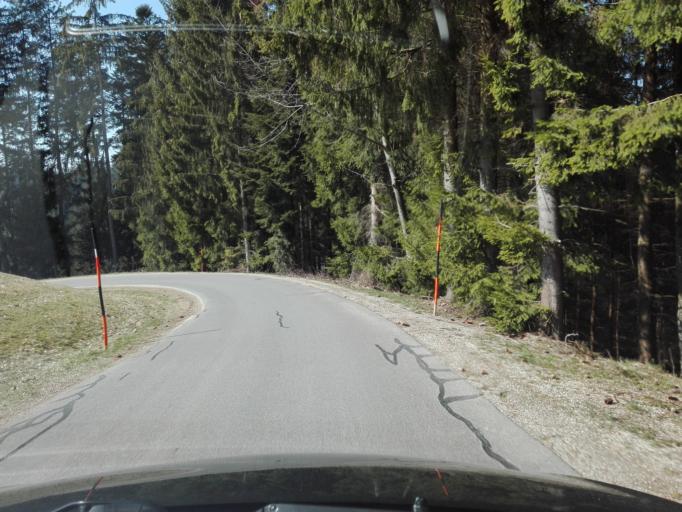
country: AT
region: Upper Austria
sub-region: Politischer Bezirk Perg
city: Bad Kreuzen
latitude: 48.3487
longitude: 14.7231
